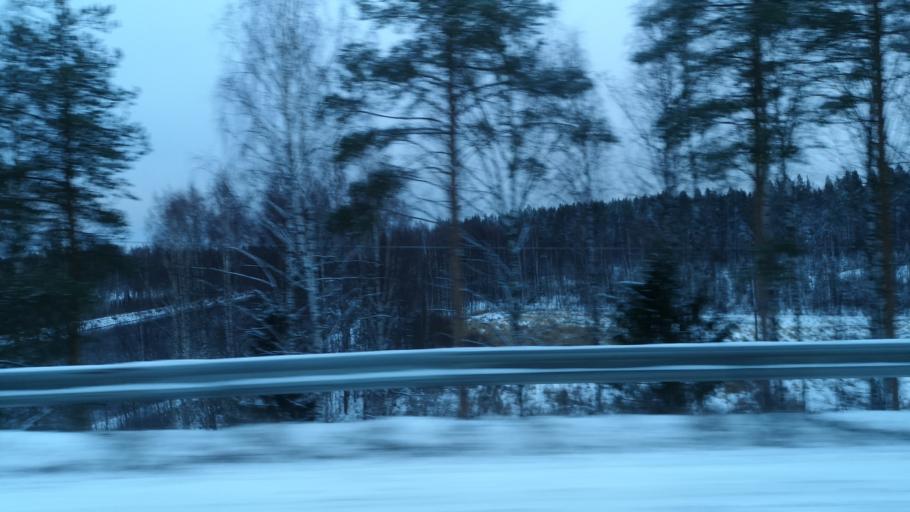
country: FI
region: Southern Savonia
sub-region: Savonlinna
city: Enonkoski
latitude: 62.0978
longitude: 28.6631
